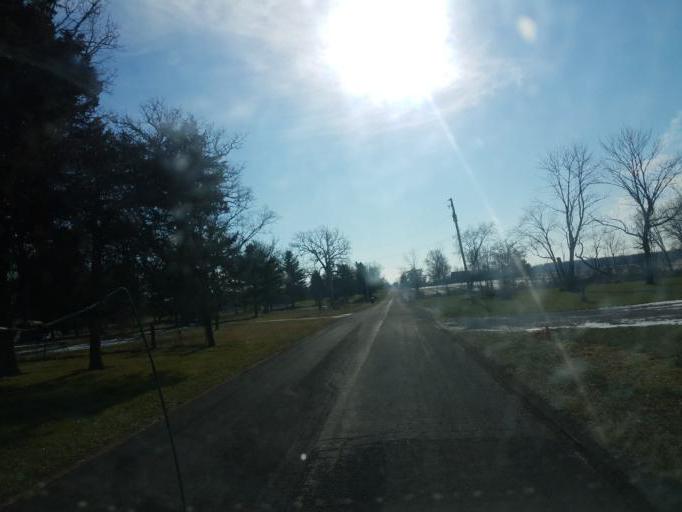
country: US
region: Ohio
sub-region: Morrow County
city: Cardington
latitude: 40.4703
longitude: -82.8702
